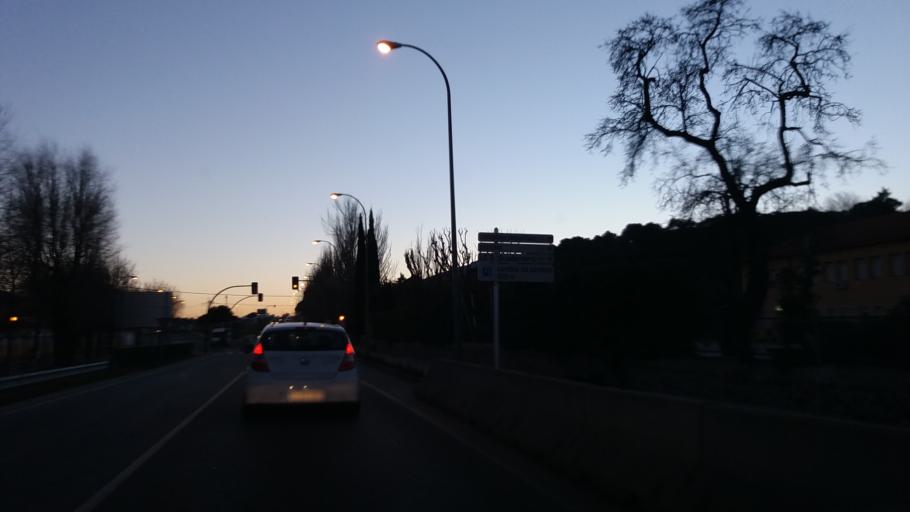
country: ES
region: Madrid
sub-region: Provincia de Madrid
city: Guadarrama
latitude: 40.6675
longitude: -4.0885
